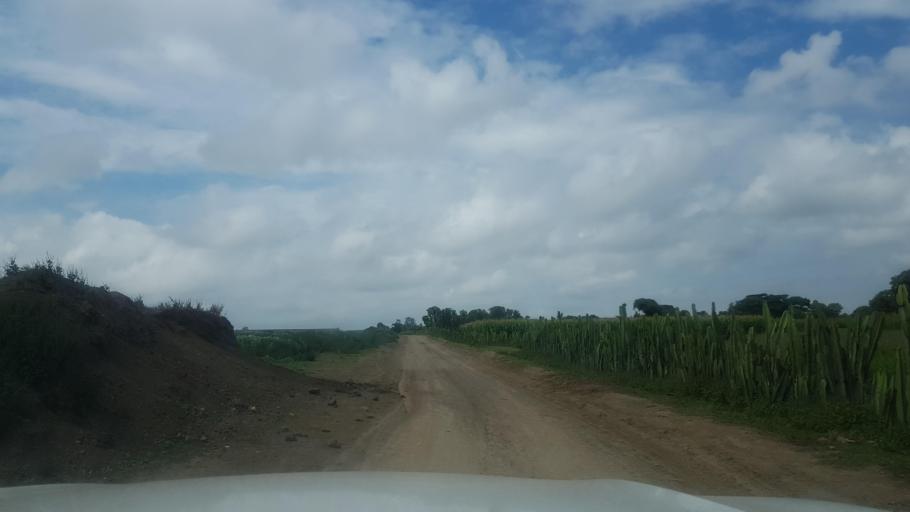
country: ET
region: Oromiya
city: Shashemene
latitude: 7.2690
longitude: 38.5982
